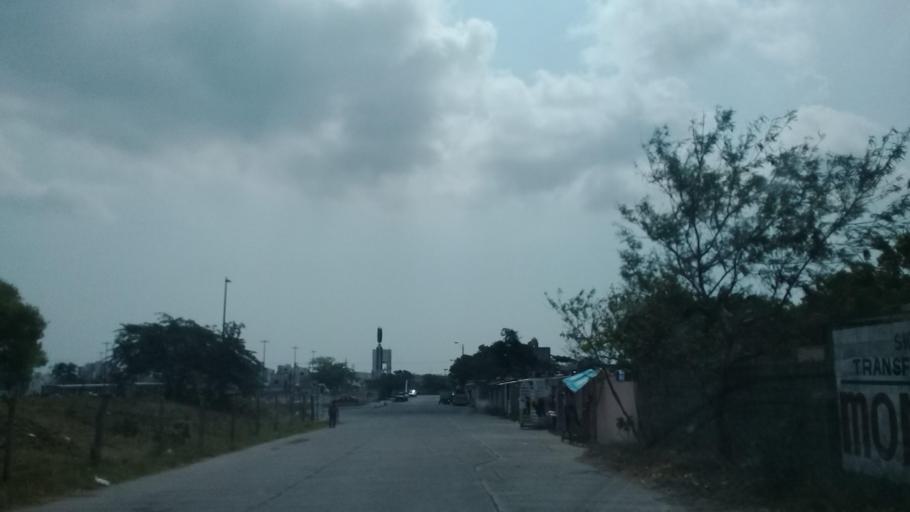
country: MX
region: Veracruz
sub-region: Veracruz
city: Hacienda Sotavento
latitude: 19.1294
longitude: -96.1797
